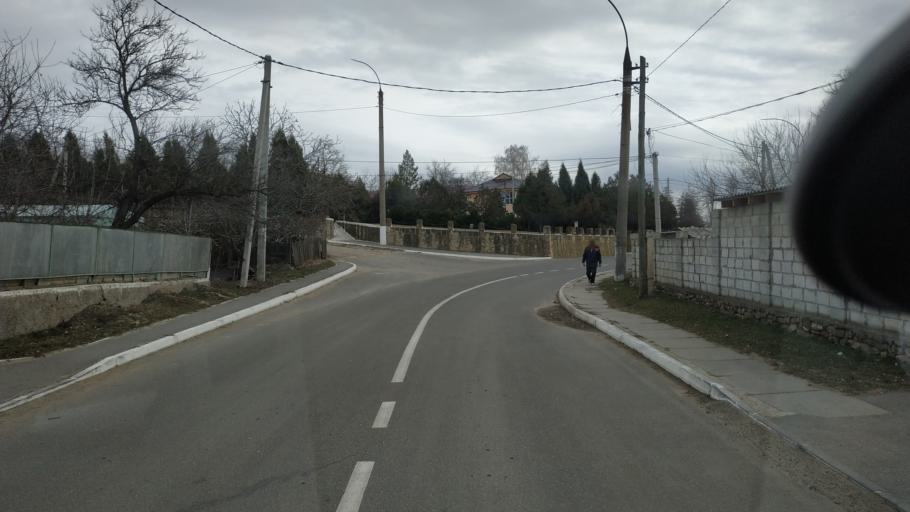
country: MD
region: Telenesti
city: Cocieri
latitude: 47.3463
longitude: 29.1121
